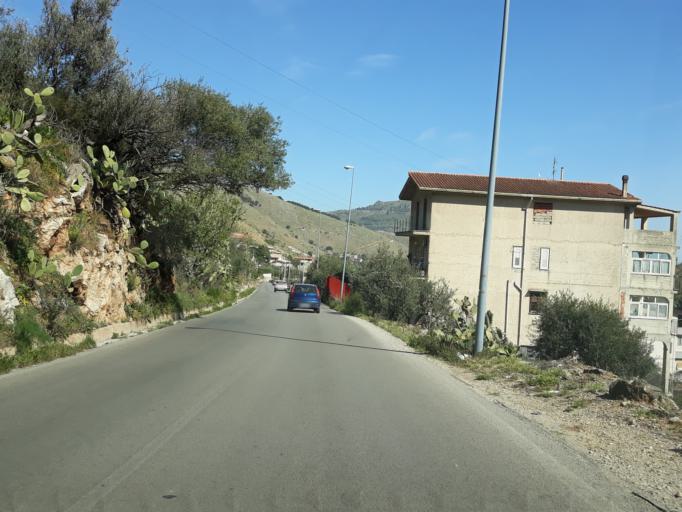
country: IT
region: Sicily
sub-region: Palermo
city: Belmonte Mezzagno
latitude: 38.0472
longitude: 13.4009
